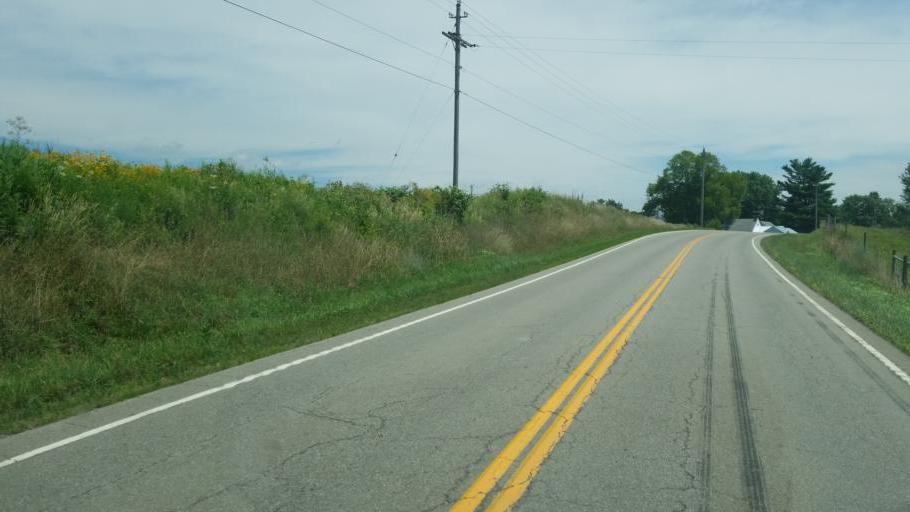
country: US
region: Ohio
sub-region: Richland County
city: Lincoln Heights
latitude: 40.8875
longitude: -82.5192
